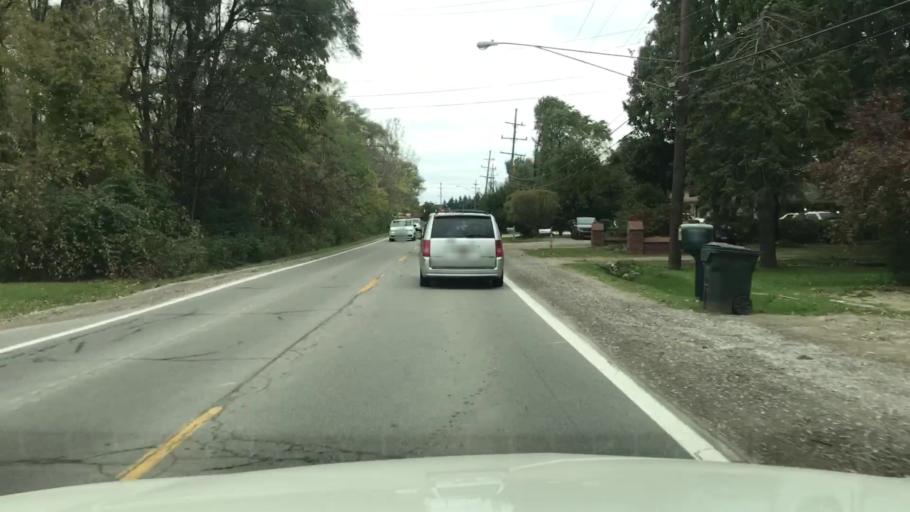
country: US
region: Michigan
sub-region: Macomb County
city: Shelby
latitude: 42.6651
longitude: -83.0735
